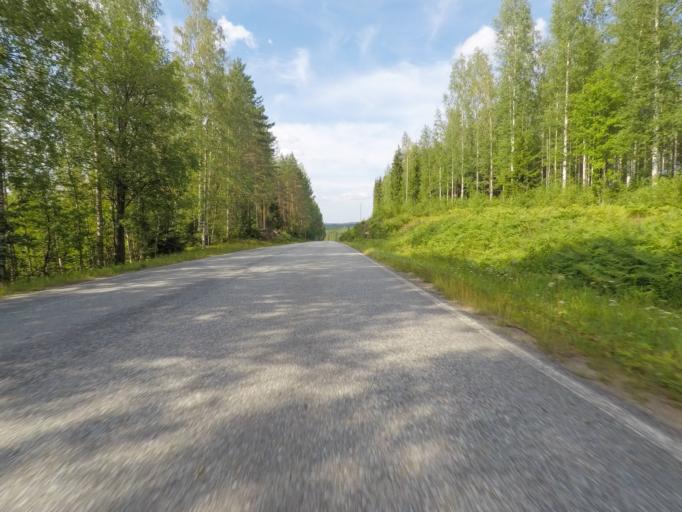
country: FI
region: Southern Savonia
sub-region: Savonlinna
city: Sulkava
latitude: 61.7117
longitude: 28.2103
